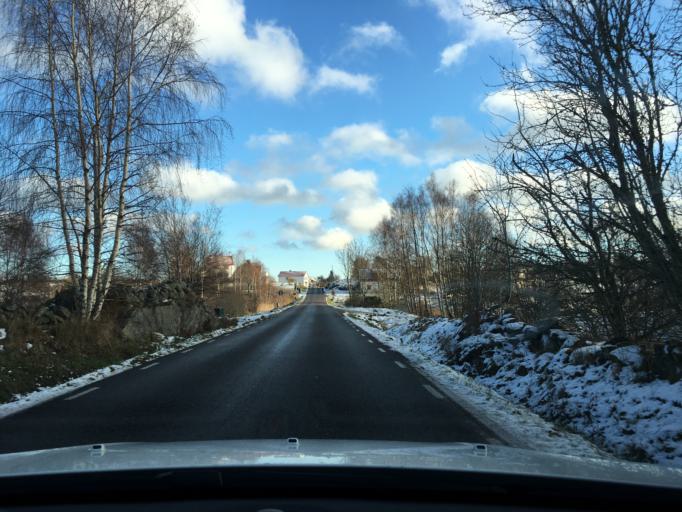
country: SE
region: Vaestra Goetaland
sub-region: Tjorns Kommun
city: Myggenas
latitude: 58.0520
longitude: 11.7064
